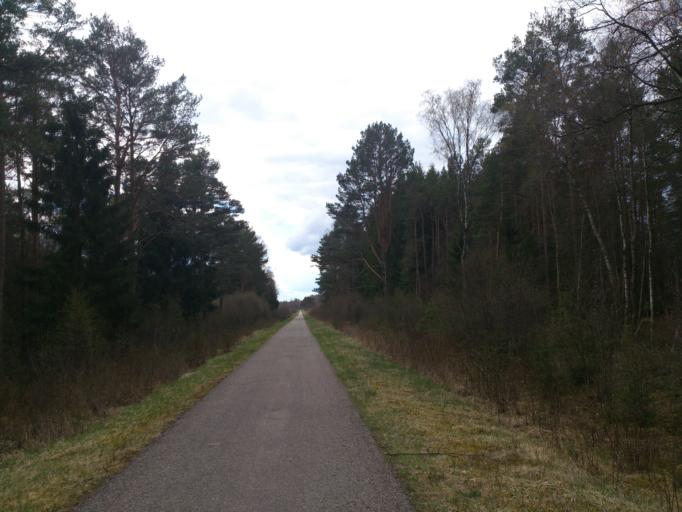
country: SE
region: Vaestra Goetaland
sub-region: Ulricehamns Kommun
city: Ulricehamn
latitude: 57.9637
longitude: 13.5141
